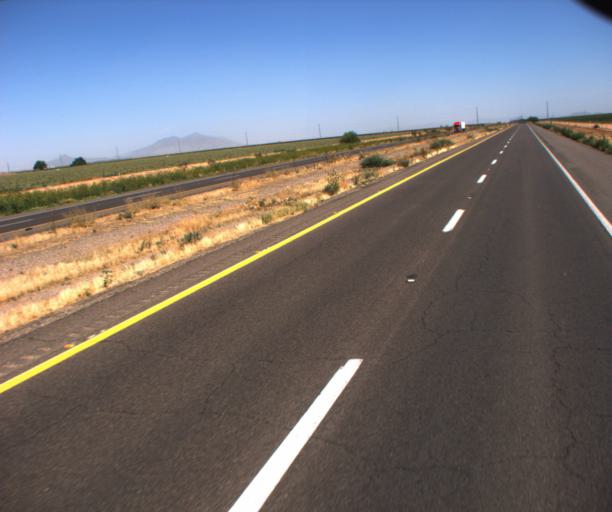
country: US
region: Arizona
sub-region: Pinal County
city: Maricopa
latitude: 32.9475
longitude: -112.0481
